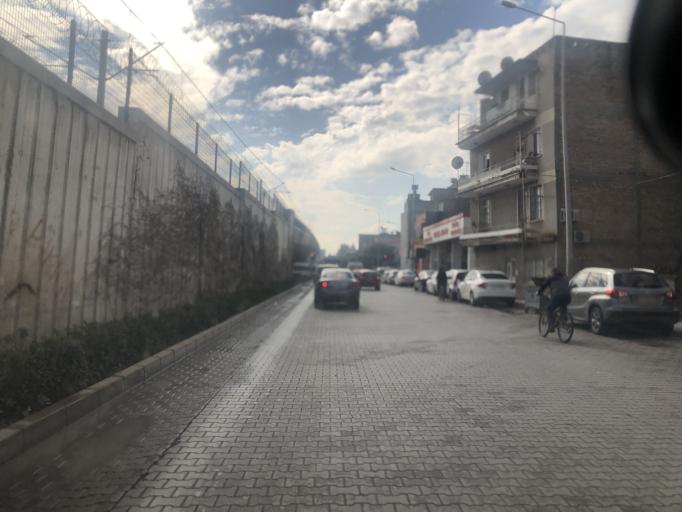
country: TR
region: Adana
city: Seyhan
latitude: 36.9887
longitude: 35.3184
